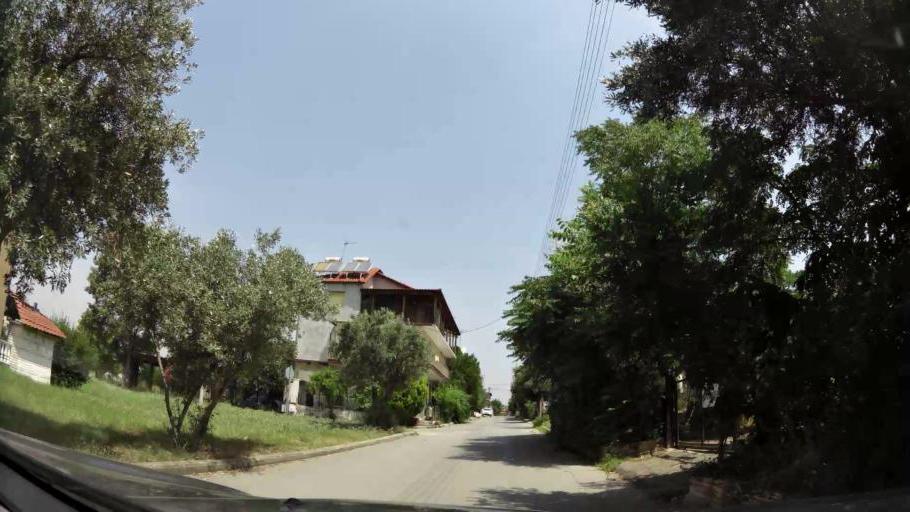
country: GR
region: Central Macedonia
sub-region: Nomos Thessalonikis
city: Evosmos
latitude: 40.6747
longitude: 22.8947
